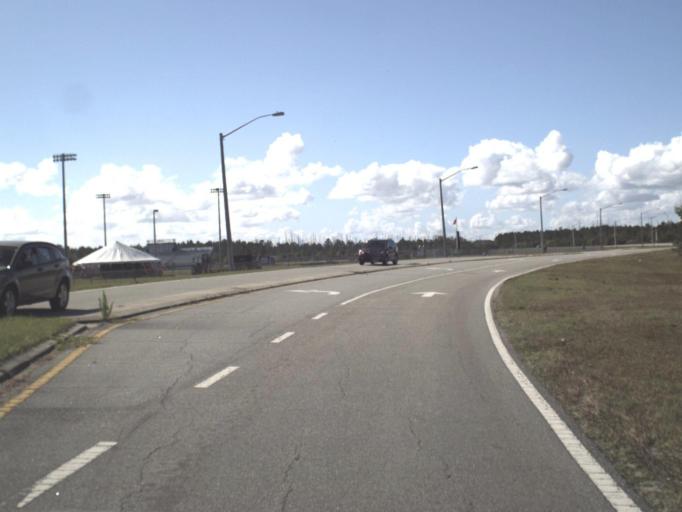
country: US
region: Florida
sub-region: Flagler County
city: Palm Coast
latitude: 29.6035
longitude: -81.2359
